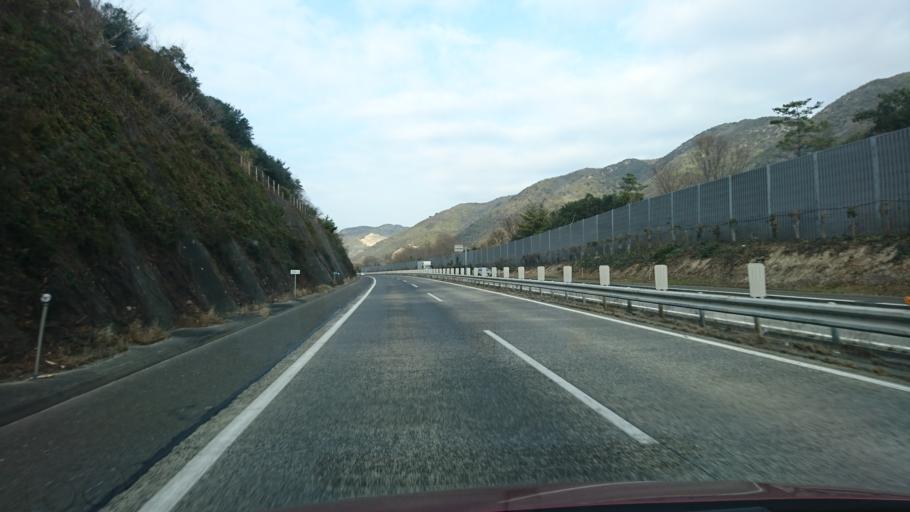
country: JP
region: Hyogo
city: Kariya
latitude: 34.7756
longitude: 134.3573
